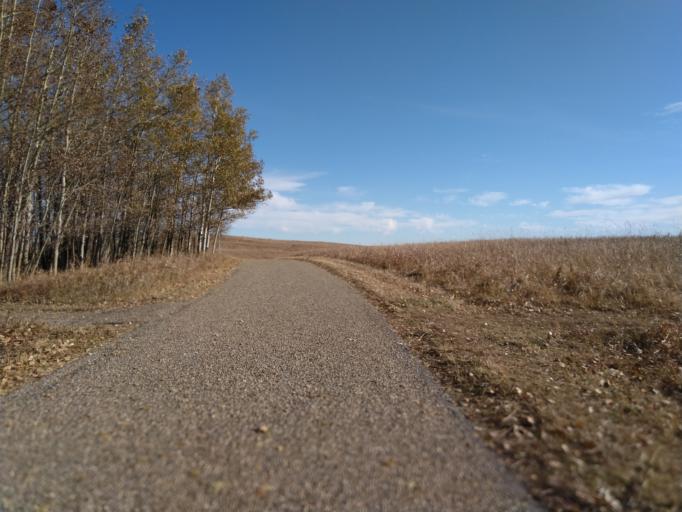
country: CA
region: Alberta
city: Calgary
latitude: 51.1236
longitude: -114.1275
